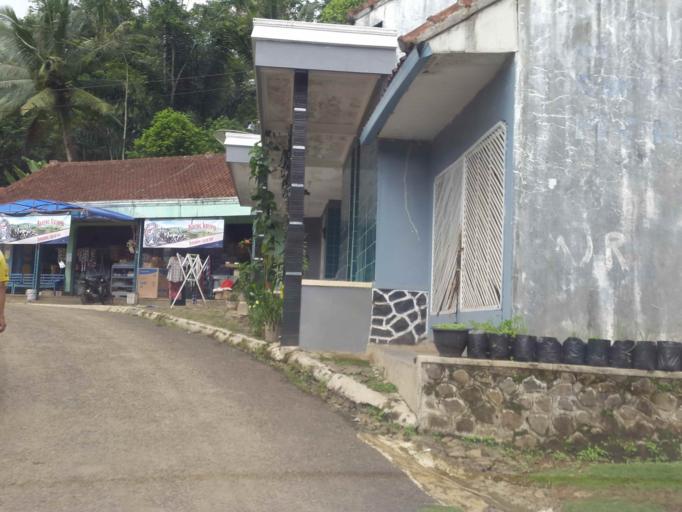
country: ID
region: Central Java
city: Cigintung
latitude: -7.2334
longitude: 108.6946
